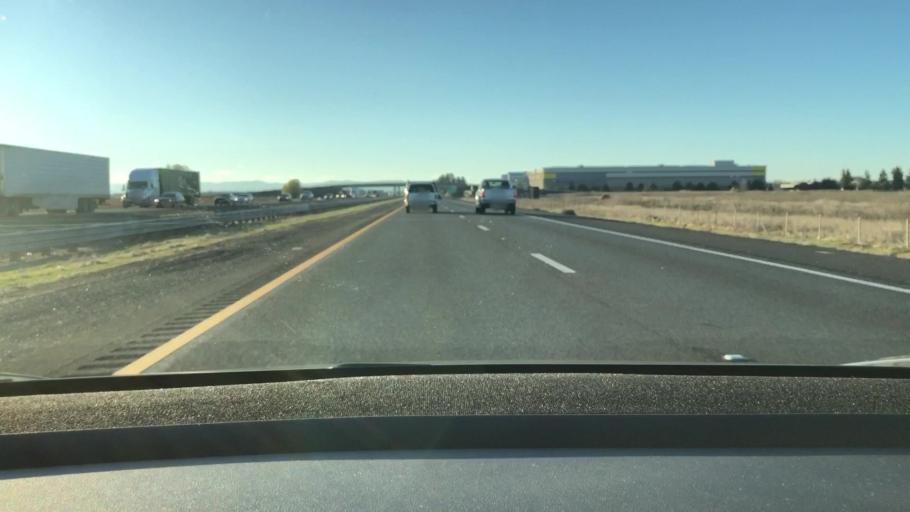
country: US
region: California
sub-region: Yolo County
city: Woodland
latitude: 38.6740
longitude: -121.7047
